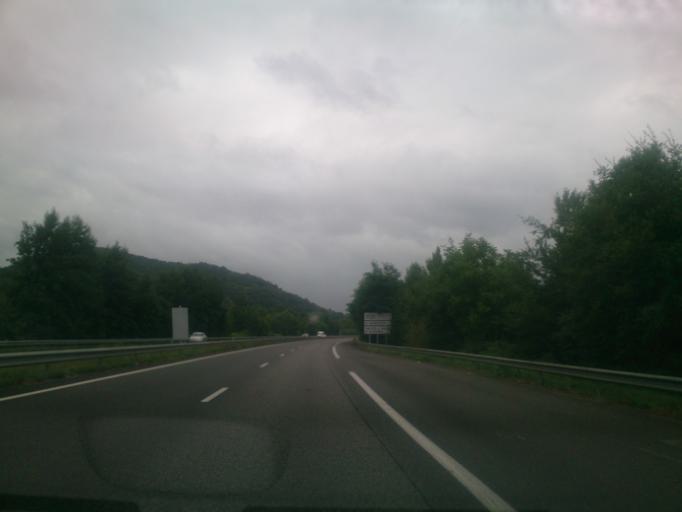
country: FR
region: Midi-Pyrenees
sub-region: Departement de la Haute-Garonne
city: Martres-Tolosane
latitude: 43.1792
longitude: 0.9789
